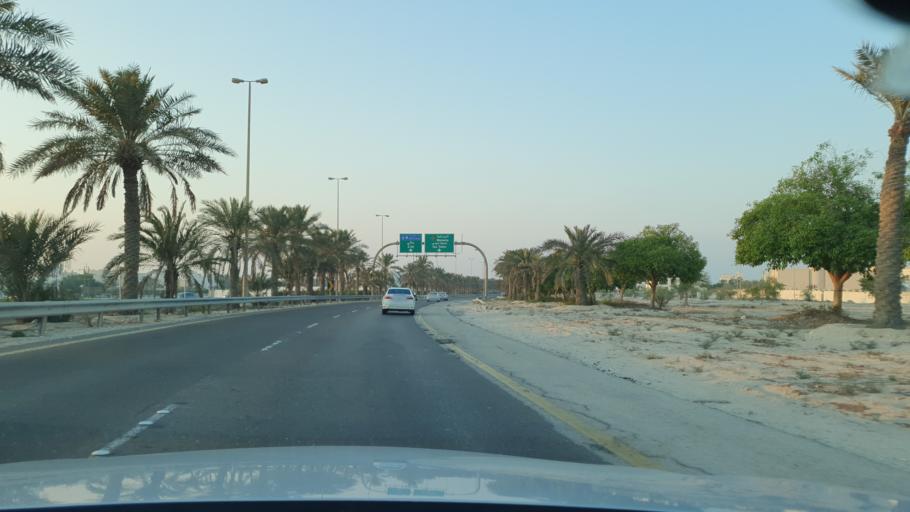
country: BH
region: Northern
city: Madinat `Isa
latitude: 26.1504
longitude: 50.5375
